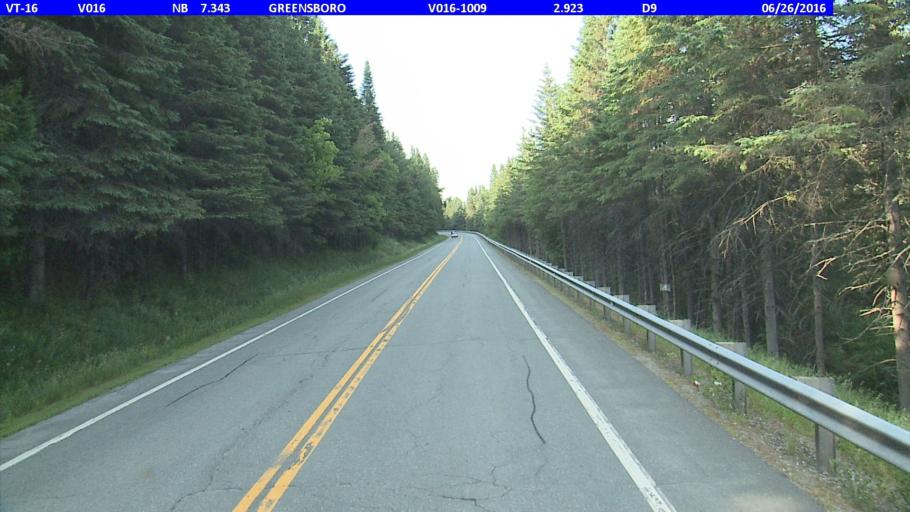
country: US
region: Vermont
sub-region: Caledonia County
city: Hardwick
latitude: 44.5816
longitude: -72.2414
